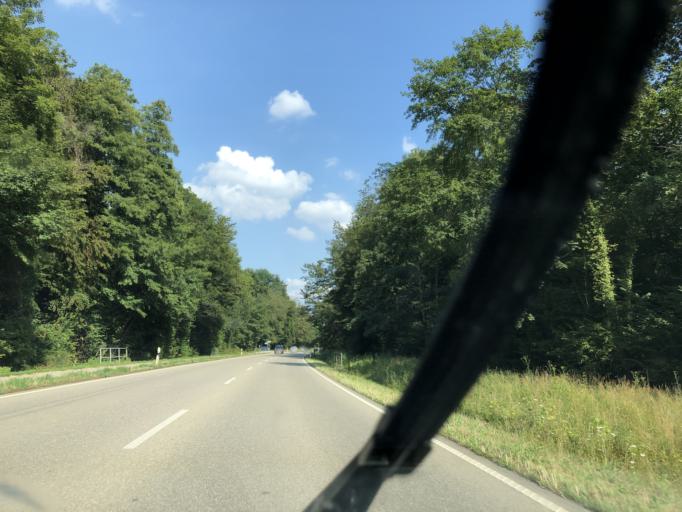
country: DE
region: Baden-Wuerttemberg
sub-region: Freiburg Region
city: Kehl
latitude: 48.4958
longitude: 7.8104
